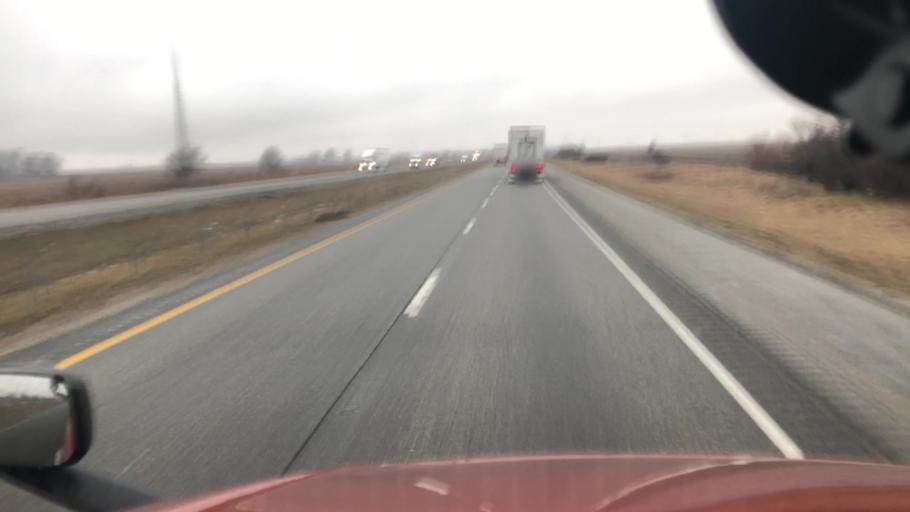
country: US
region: Indiana
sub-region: White County
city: Wolcott
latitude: 40.6837
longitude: -87.0553
